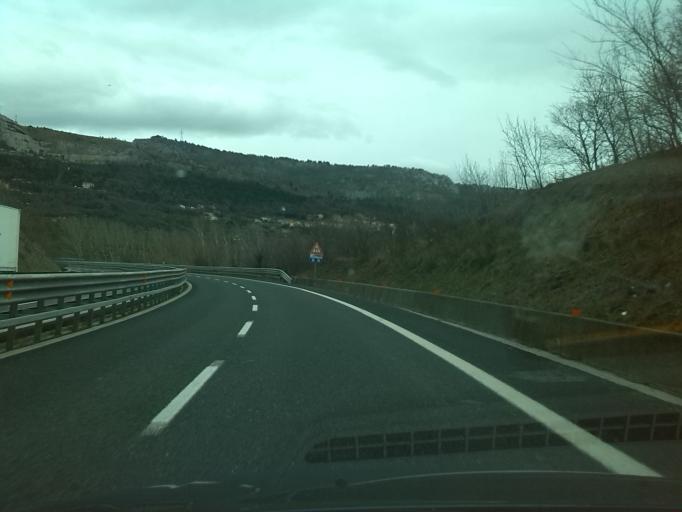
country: IT
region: Friuli Venezia Giulia
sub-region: Provincia di Trieste
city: Dolina
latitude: 45.6150
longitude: 13.8492
